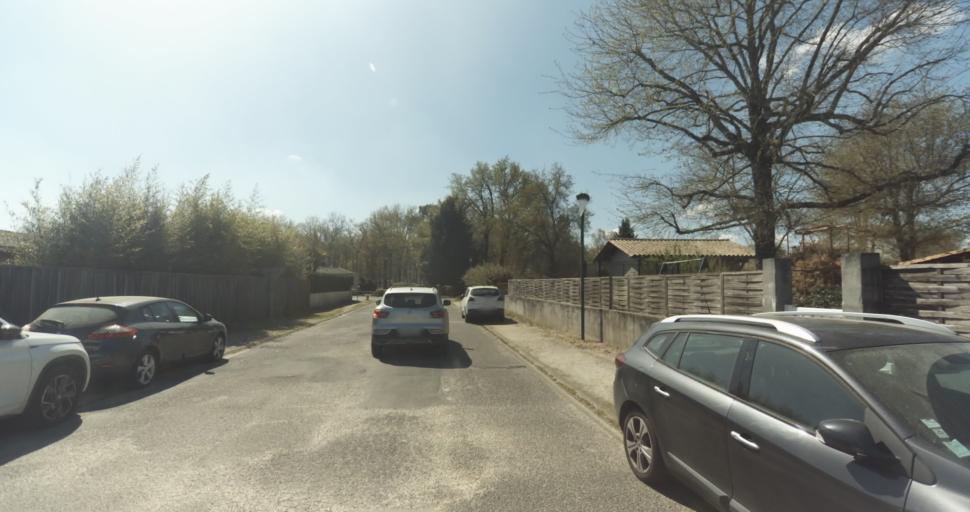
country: FR
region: Aquitaine
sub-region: Departement de la Gironde
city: Martignas-sur-Jalle
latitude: 44.8069
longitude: -0.7894
